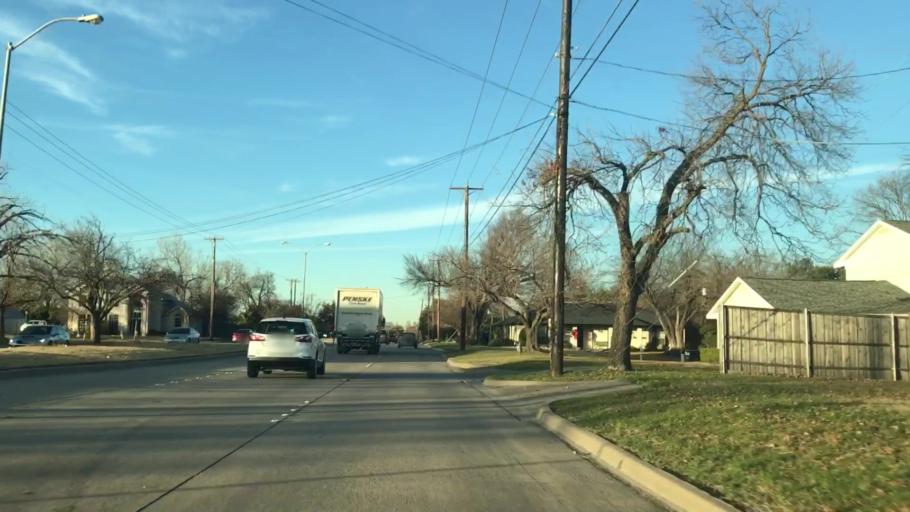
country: US
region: Texas
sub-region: Dallas County
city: Rowlett
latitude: 32.8860
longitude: -96.5182
